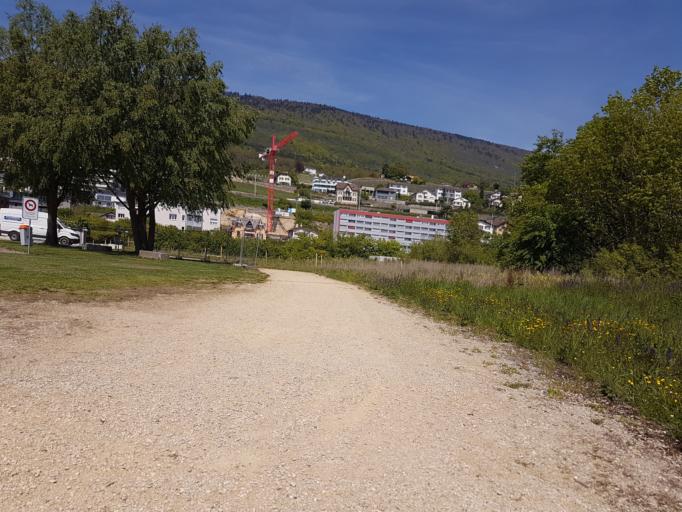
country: CH
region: Neuchatel
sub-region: Neuchatel District
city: Saint-Blaise
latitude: 47.0100
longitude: 6.9770
